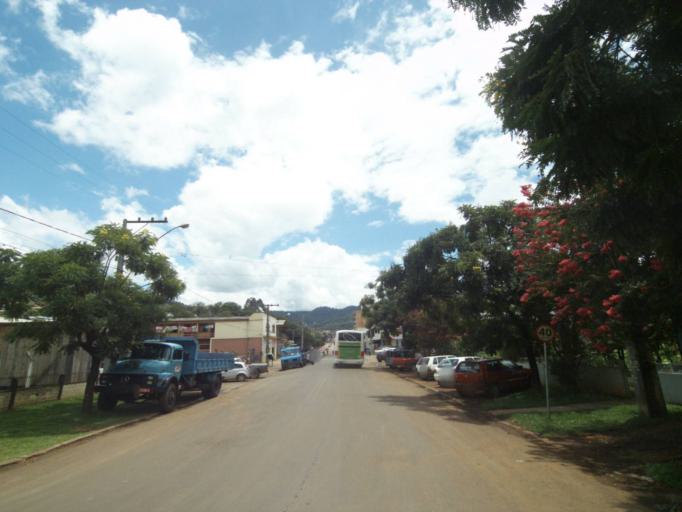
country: BR
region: Parana
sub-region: Uniao Da Vitoria
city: Uniao da Vitoria
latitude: -26.1569
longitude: -51.5531
